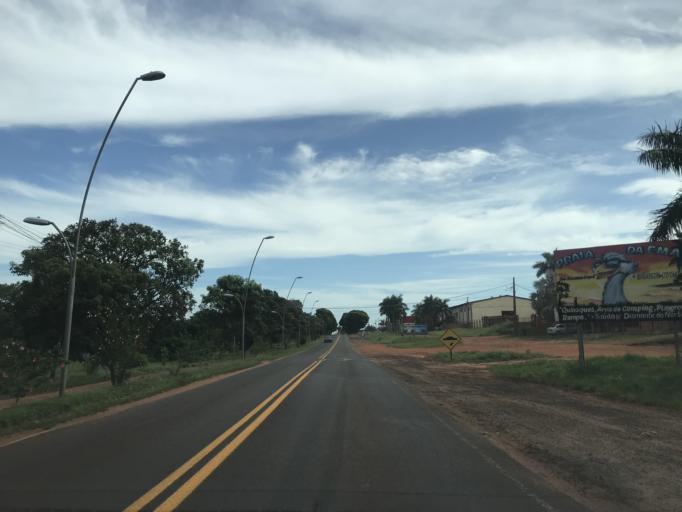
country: BR
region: Parana
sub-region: Terra Rica
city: Terra Rica
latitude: -22.7397
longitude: -52.6247
